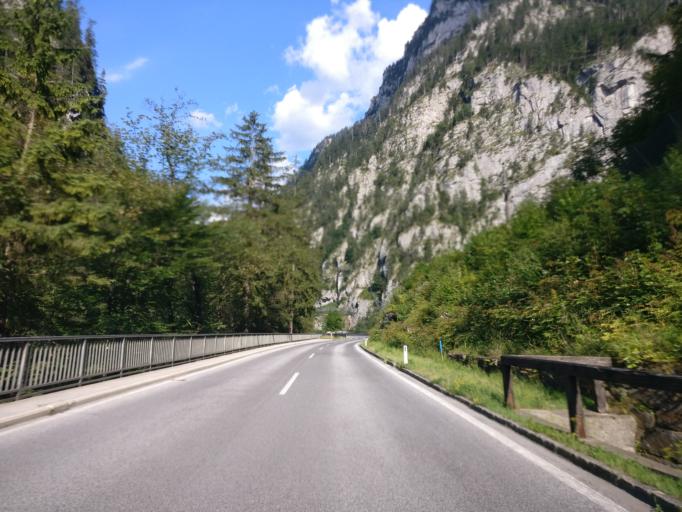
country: AT
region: Styria
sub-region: Politischer Bezirk Leoben
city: Hieflau
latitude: 47.5919
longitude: 14.7014
